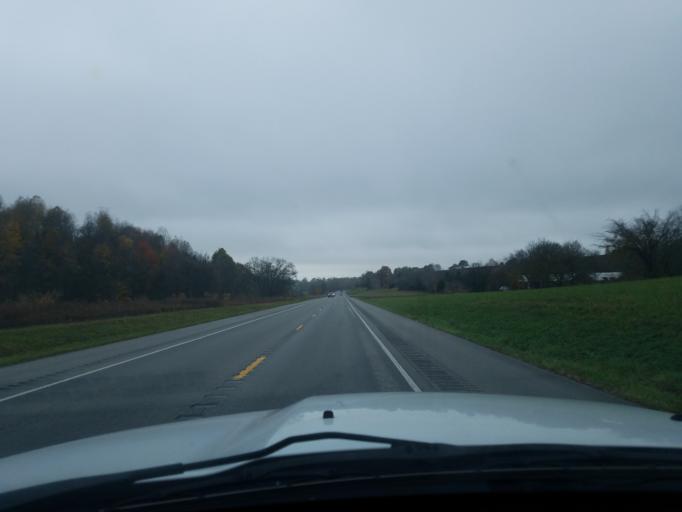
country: US
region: Kentucky
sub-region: Taylor County
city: Campbellsville
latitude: 37.3923
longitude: -85.4408
